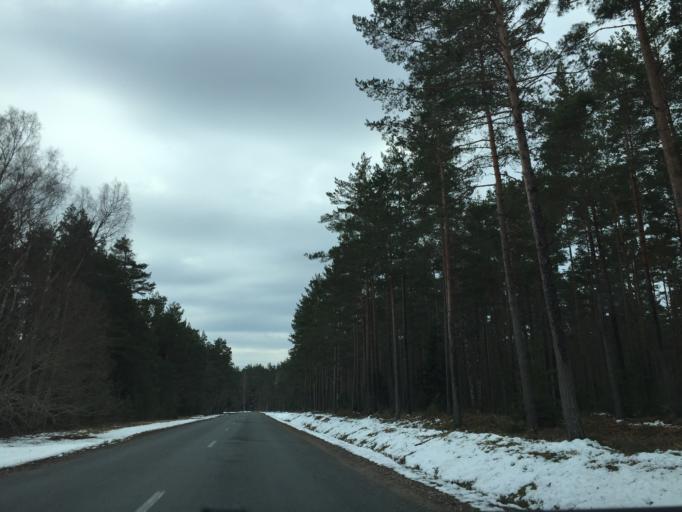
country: EE
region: Saare
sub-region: Kuressaare linn
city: Kuressaare
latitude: 58.4207
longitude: 22.0747
